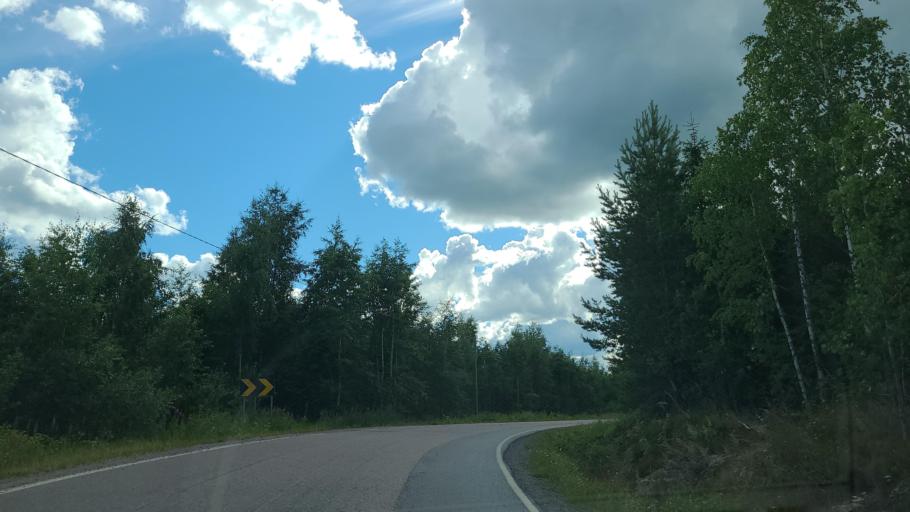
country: FI
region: Central Finland
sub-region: Jaemsae
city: Jaemsae
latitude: 61.9035
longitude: 25.2792
